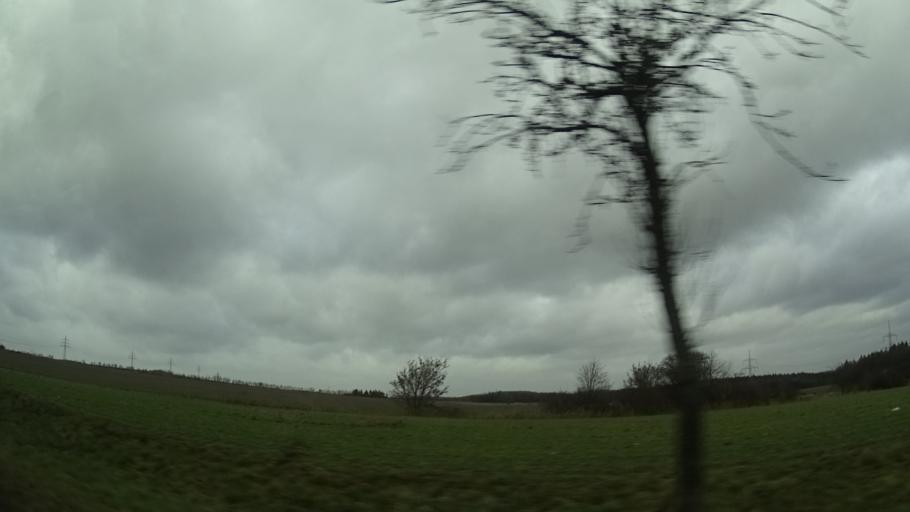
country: DE
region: Thuringia
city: Auma
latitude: 50.6838
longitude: 11.9159
